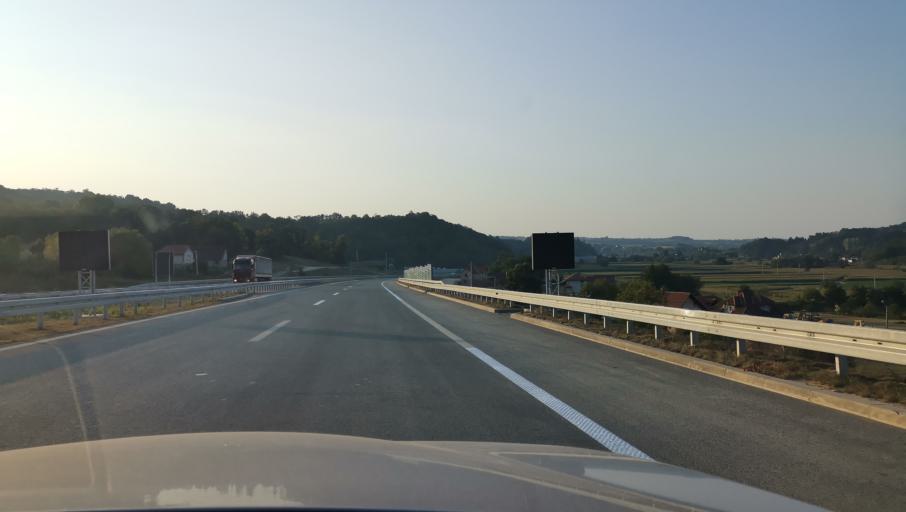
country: RS
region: Central Serbia
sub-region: Kolubarski Okrug
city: Ljig
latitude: 44.2152
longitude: 20.2601
